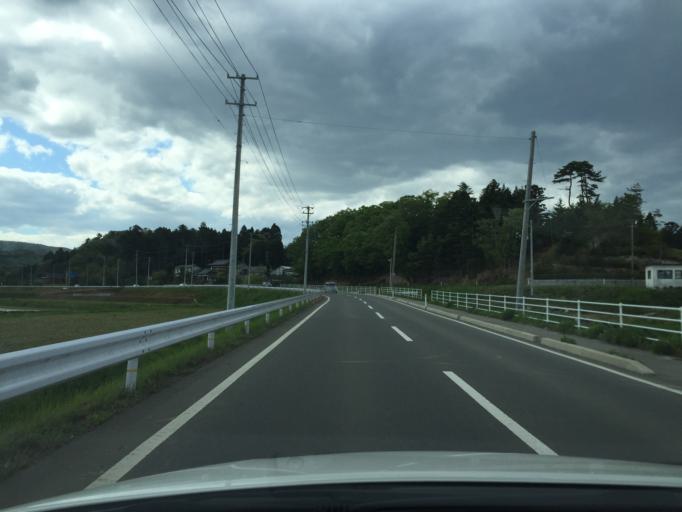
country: JP
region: Miyagi
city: Marumori
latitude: 37.7360
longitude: 140.9247
